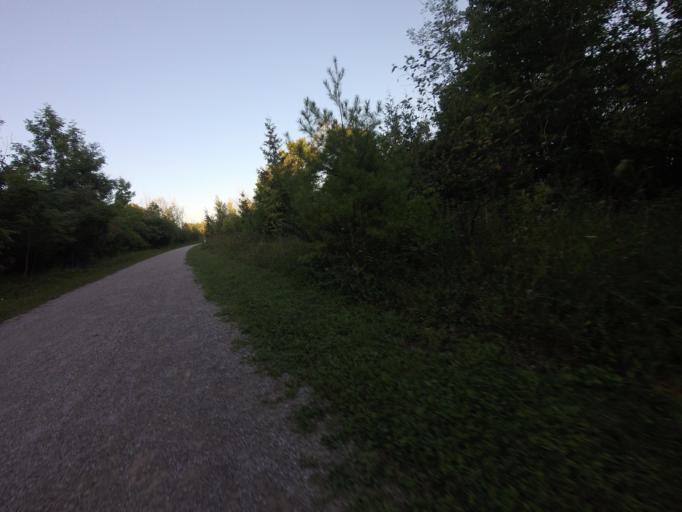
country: CA
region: Ontario
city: Goderich
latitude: 43.7599
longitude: -81.7082
